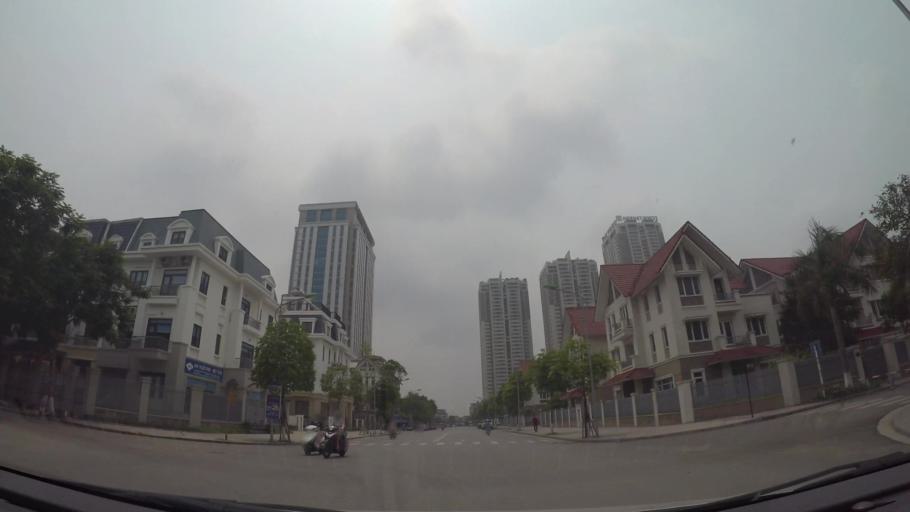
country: VN
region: Ha Noi
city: Ha Dong
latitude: 20.9754
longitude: 105.7567
